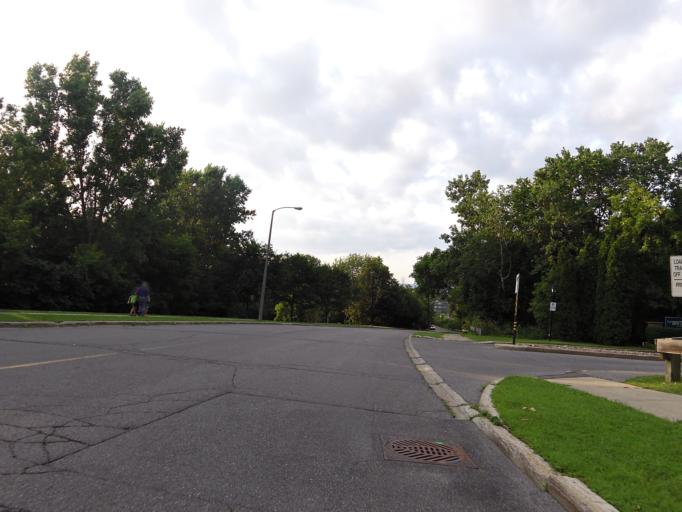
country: CA
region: Ontario
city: Bells Corners
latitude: 45.3599
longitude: -75.7955
